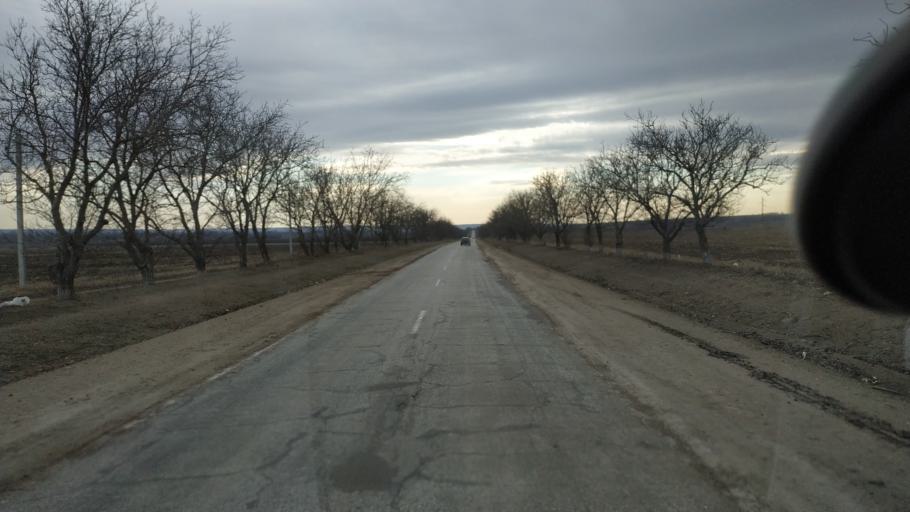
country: MD
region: Criuleni
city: Criuleni
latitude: 47.1952
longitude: 29.1498
